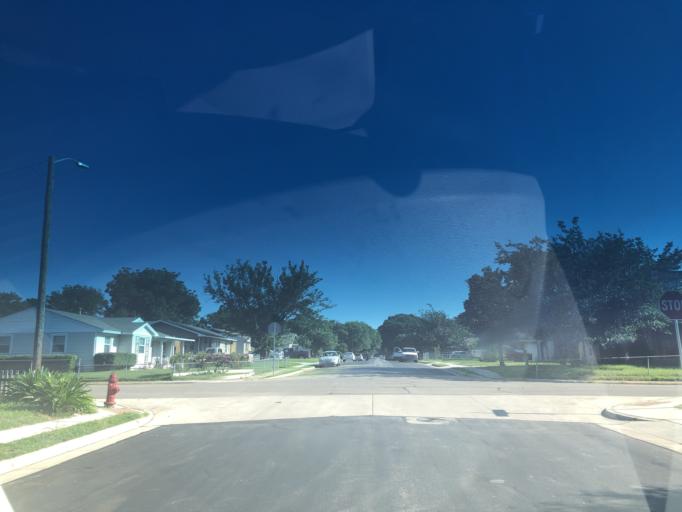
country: US
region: Texas
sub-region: Dallas County
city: Grand Prairie
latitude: 32.7289
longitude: -97.0374
